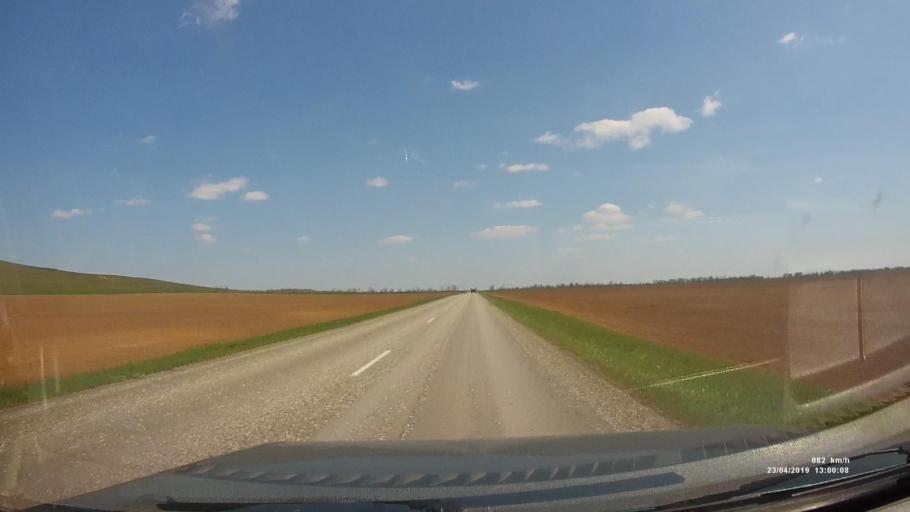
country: RU
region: Kalmykiya
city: Yashalta
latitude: 46.6042
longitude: 42.6276
